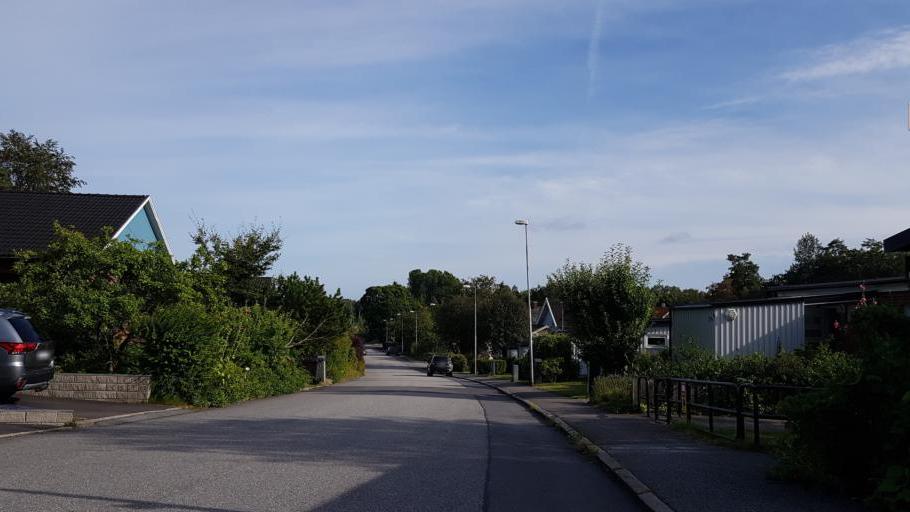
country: SE
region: Vaestra Goetaland
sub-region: Molndal
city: Moelndal
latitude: 57.6680
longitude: 12.0328
